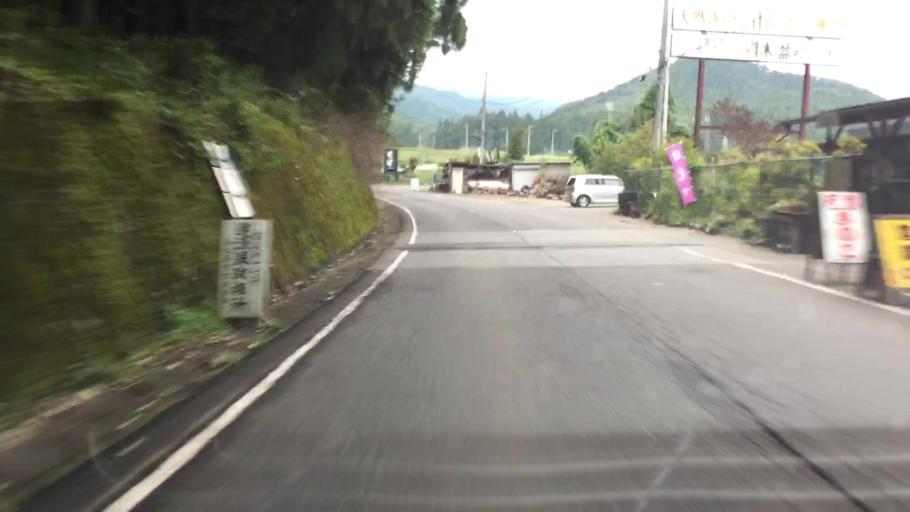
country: JP
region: Tochigi
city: Imaichi
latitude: 36.7622
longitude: 139.6795
